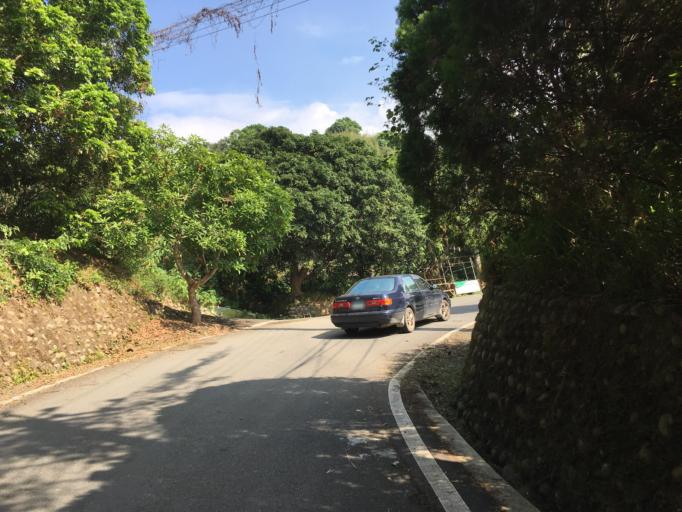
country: TW
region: Taiwan
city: Fengyuan
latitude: 24.1793
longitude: 120.7829
